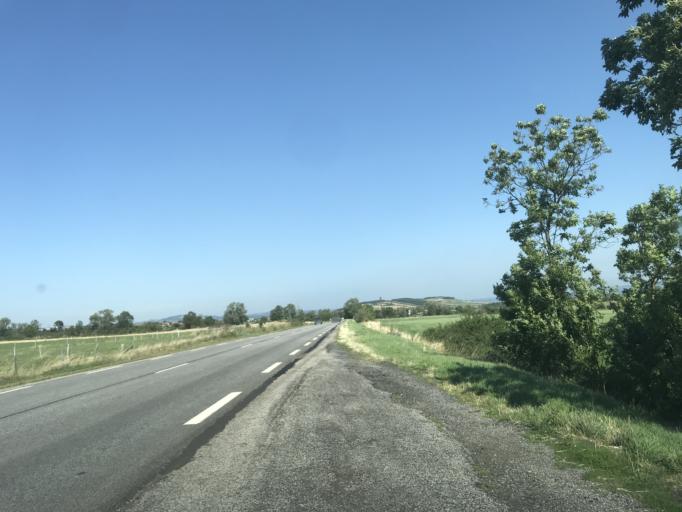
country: FR
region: Auvergne
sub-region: Departement de la Haute-Loire
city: Bains
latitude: 44.9981
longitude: 3.8168
